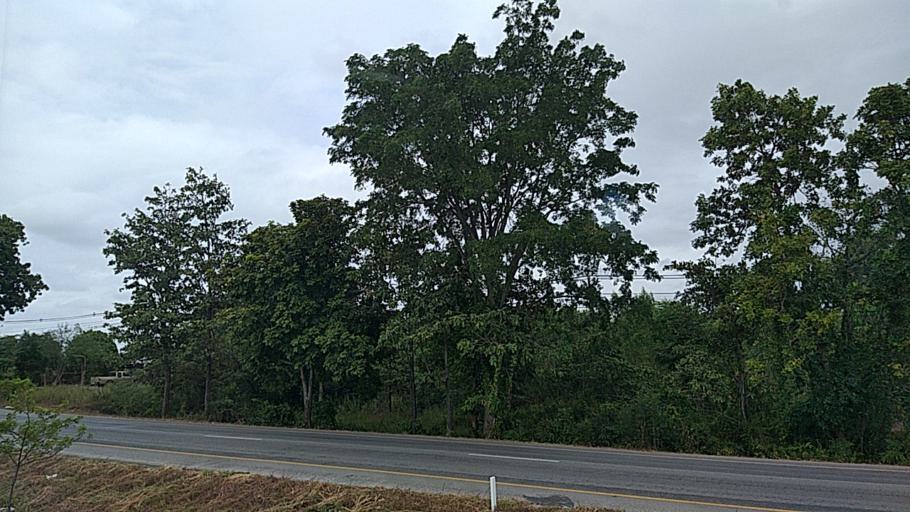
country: TH
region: Maha Sarakham
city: Kut Rang
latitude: 16.0506
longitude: 102.9562
